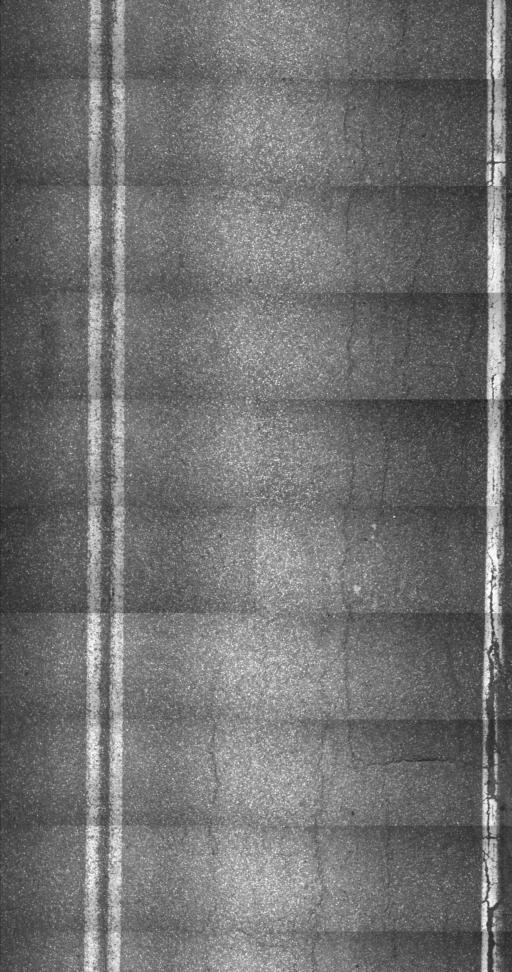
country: US
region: Vermont
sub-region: Orange County
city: Randolph
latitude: 43.9388
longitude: -72.6546
